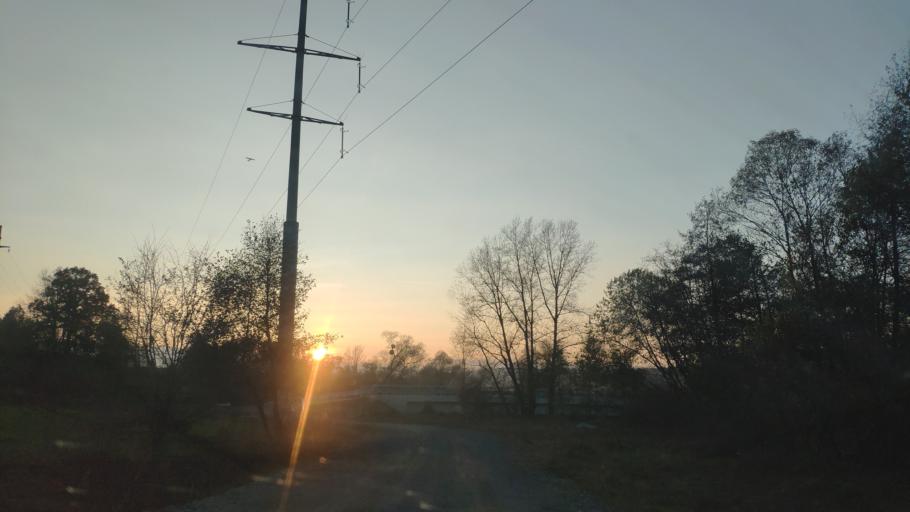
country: RO
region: Mures
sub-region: Comuna Chibed
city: Chibed
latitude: 46.5362
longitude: 24.9816
